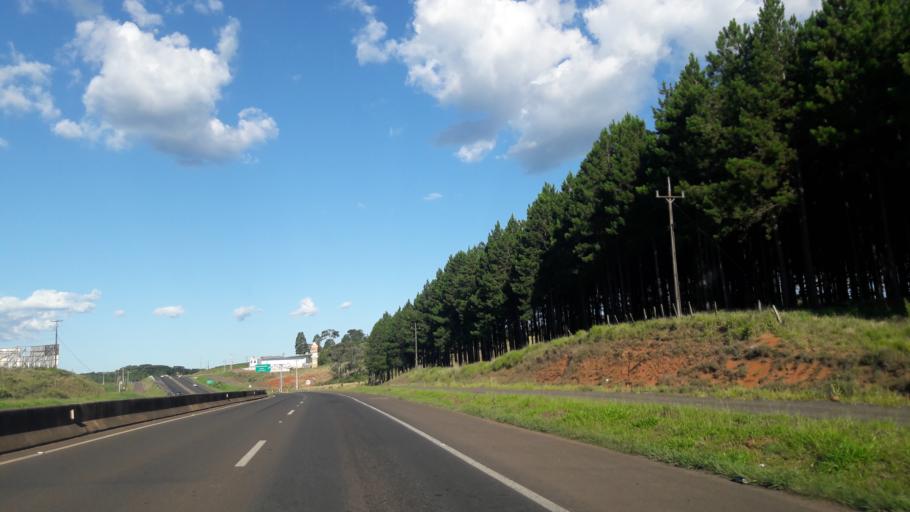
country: BR
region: Parana
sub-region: Guarapuava
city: Guarapuava
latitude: -25.3432
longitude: -51.4365
